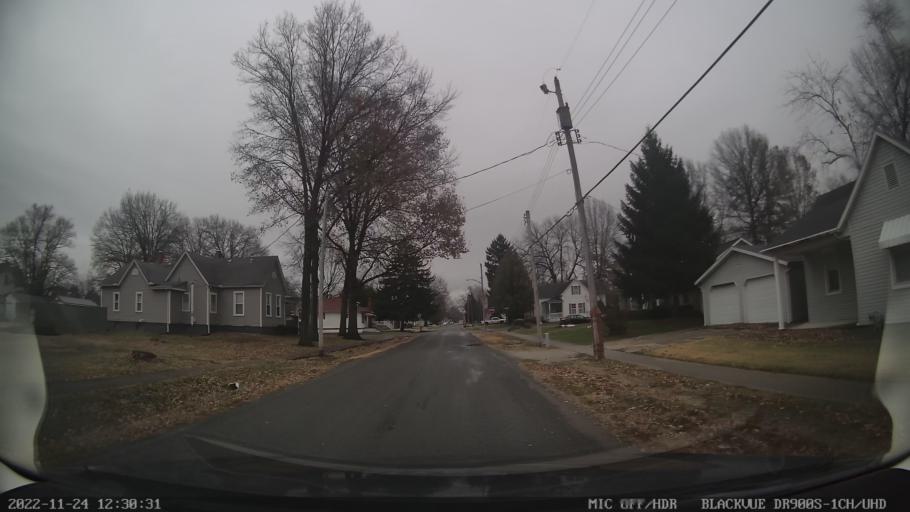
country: US
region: Illinois
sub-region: Macoupin County
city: Staunton
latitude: 39.0160
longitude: -89.7855
